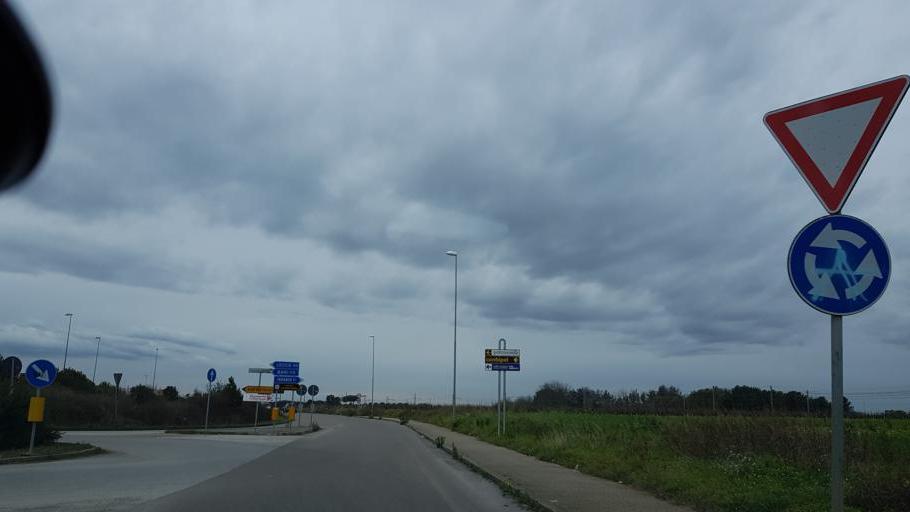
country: IT
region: Apulia
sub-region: Provincia di Brindisi
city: Brindisi
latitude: 40.6245
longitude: 17.9102
